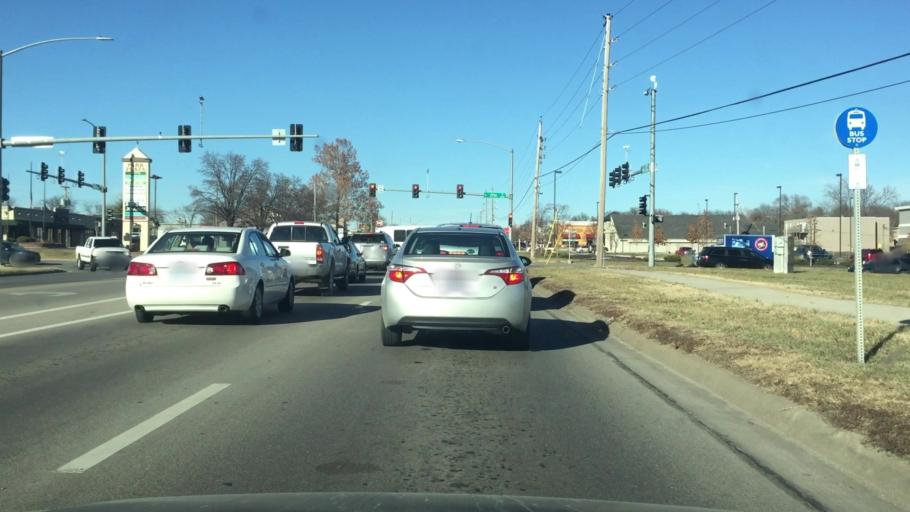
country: US
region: Kansas
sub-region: Douglas County
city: Lawrence
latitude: 38.9339
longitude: -95.2605
